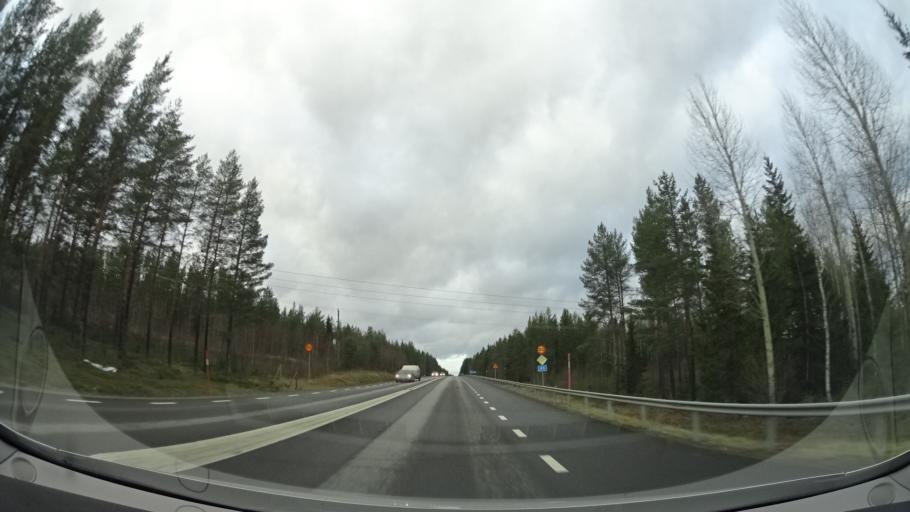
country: SE
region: Vaesterbotten
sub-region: Skelleftea Kommun
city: Viken
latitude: 64.7637
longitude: 20.8774
